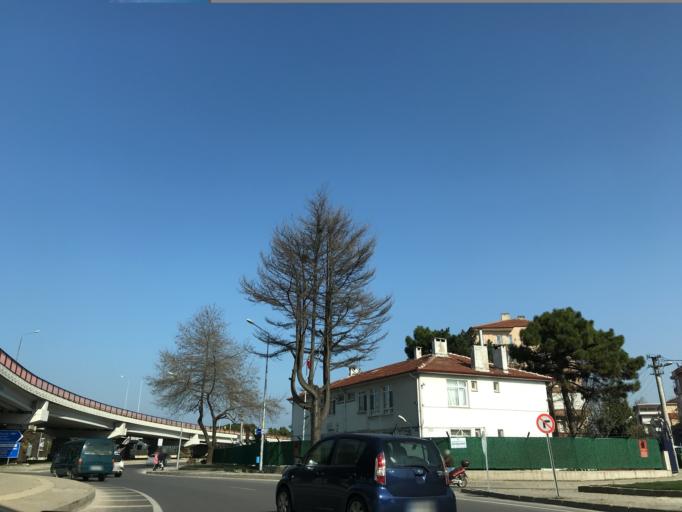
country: TR
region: Yalova
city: Yalova
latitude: 40.6562
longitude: 29.2840
